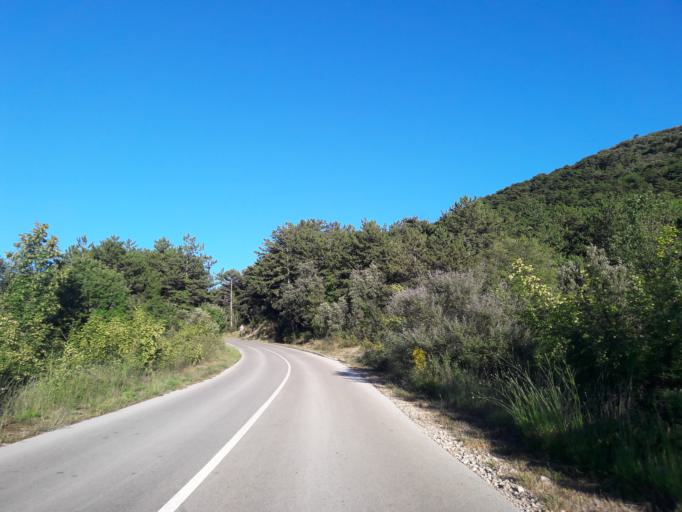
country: HR
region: Dubrovacko-Neretvanska
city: Orebic
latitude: 43.0001
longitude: 17.2504
